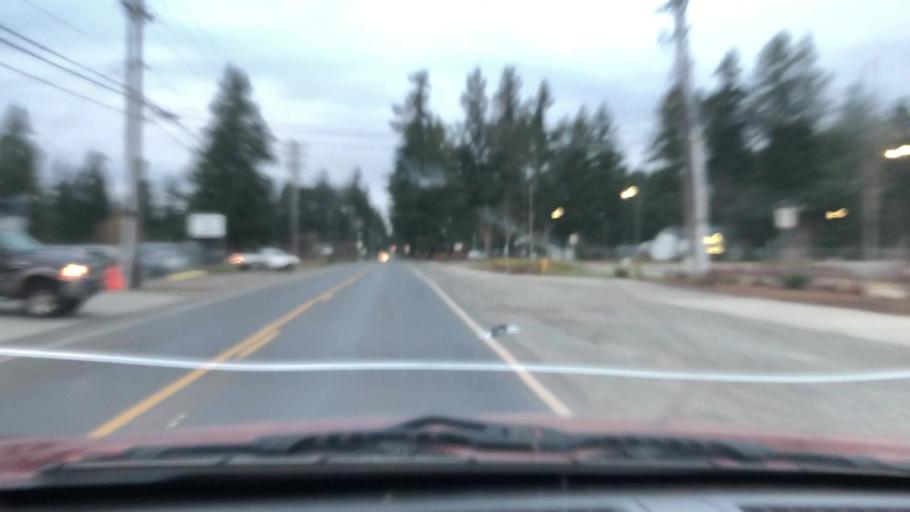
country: US
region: Washington
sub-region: Pierce County
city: Elk Plain
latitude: 47.0568
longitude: -122.4003
